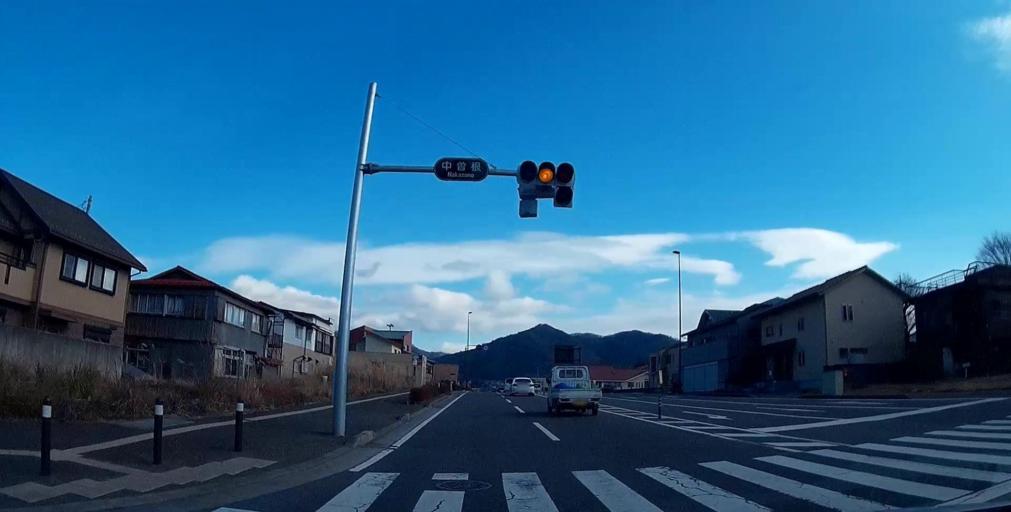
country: JP
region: Yamanashi
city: Fujikawaguchiko
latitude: 35.4864
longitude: 138.8003
